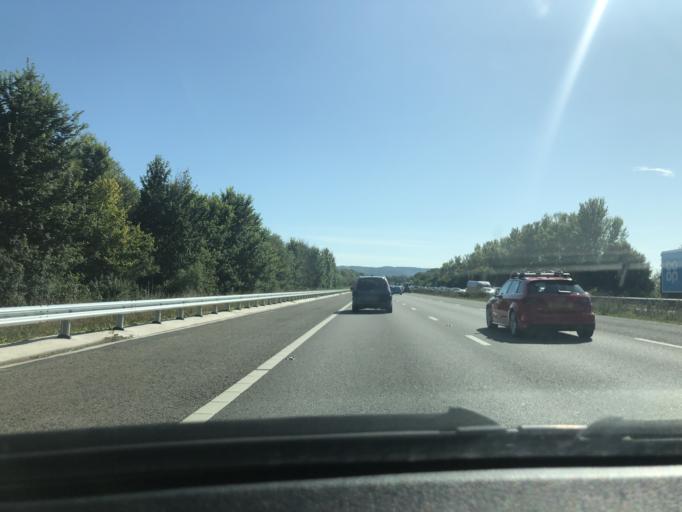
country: GB
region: England
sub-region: Somerset
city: Creech Saint Michael
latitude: 51.0120
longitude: -3.0675
